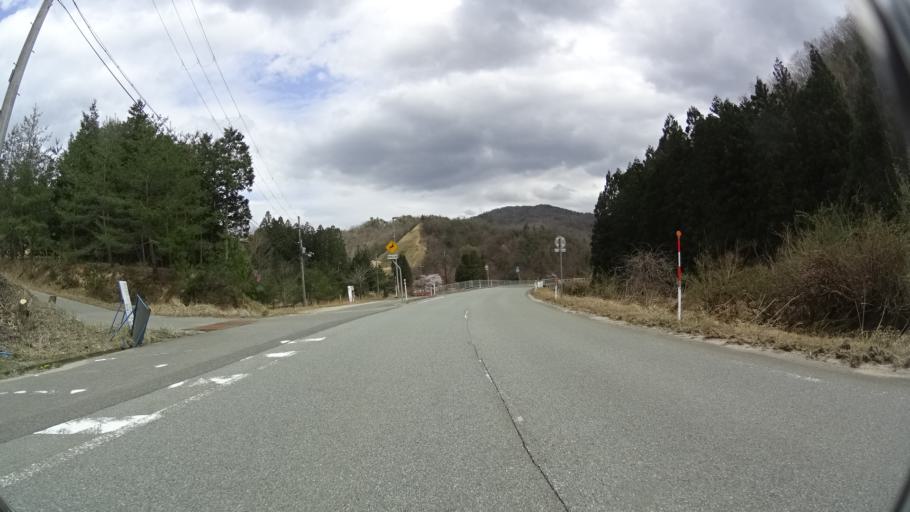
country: JP
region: Hyogo
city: Toyooka
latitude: 35.4891
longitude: 134.9205
